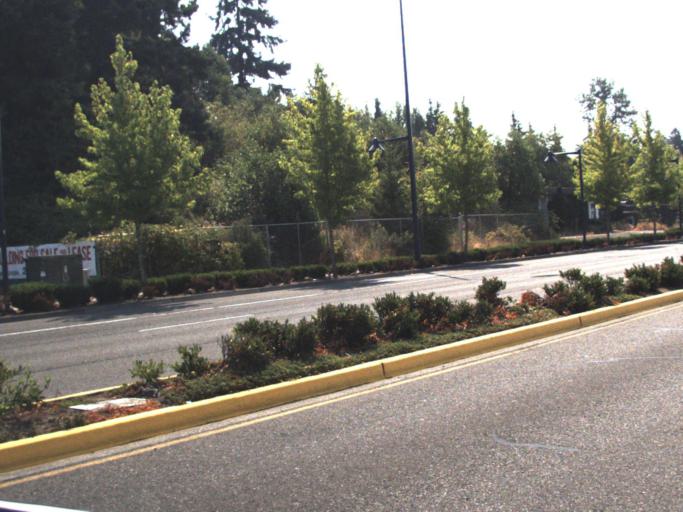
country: US
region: Washington
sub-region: King County
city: Des Moines
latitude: 47.3988
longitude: -122.2965
